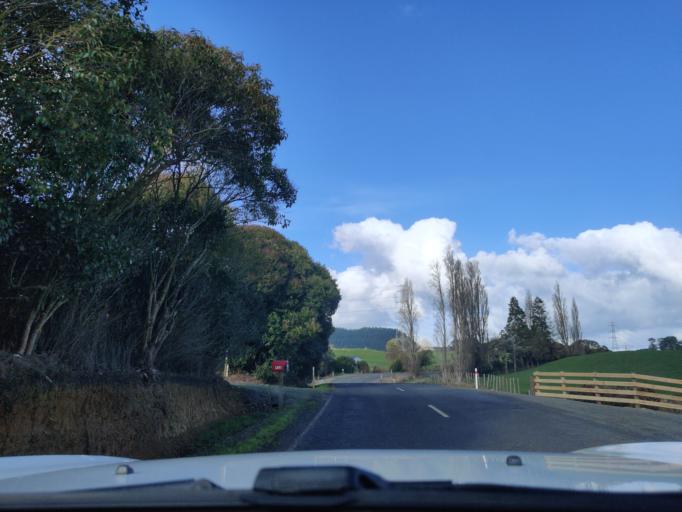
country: NZ
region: Waikato
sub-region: Waikato District
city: Te Kauwhata
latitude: -37.2862
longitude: 175.2162
